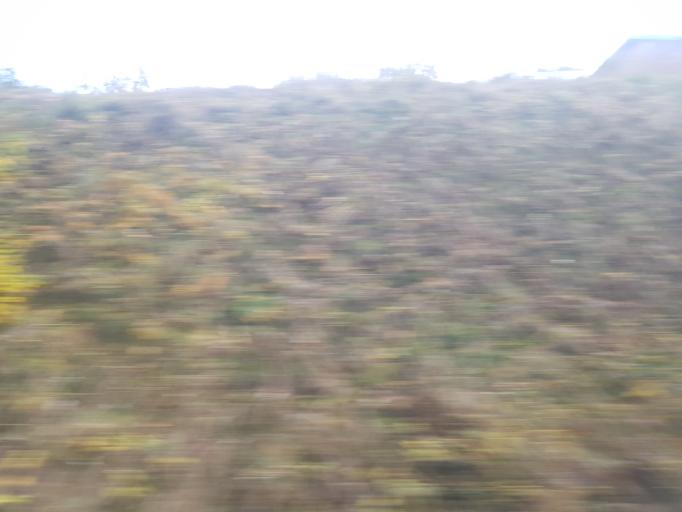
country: NO
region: Oppland
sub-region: Dovre
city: Dovre
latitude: 61.9636
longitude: 9.2632
